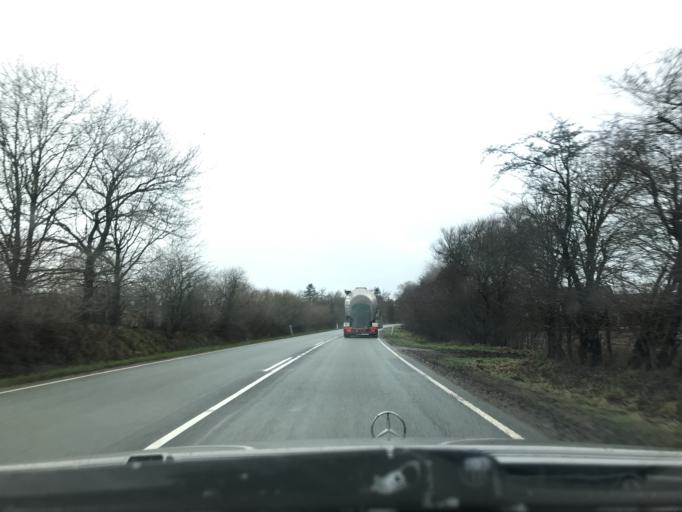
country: DK
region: South Denmark
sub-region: Esbjerg Kommune
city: Ribe
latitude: 55.2692
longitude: 8.8767
